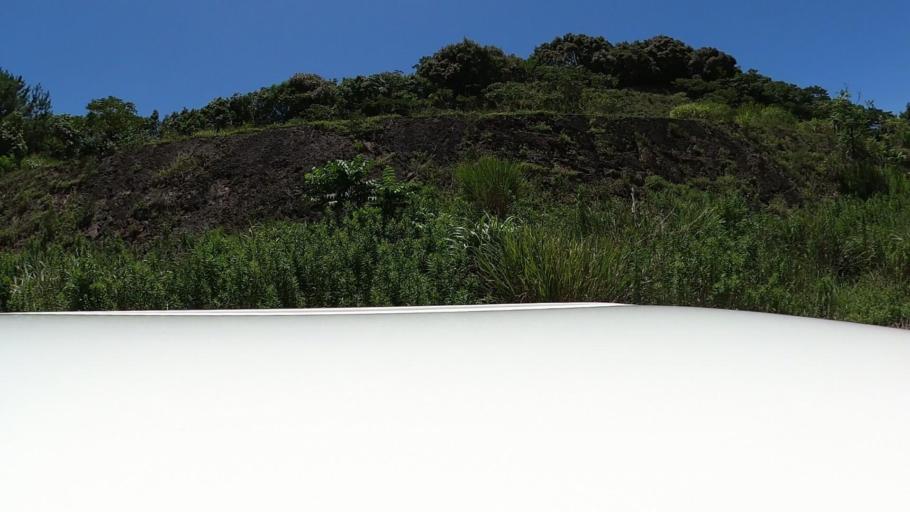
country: JP
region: Miyazaki
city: Nobeoka
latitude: 32.5365
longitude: 131.6610
